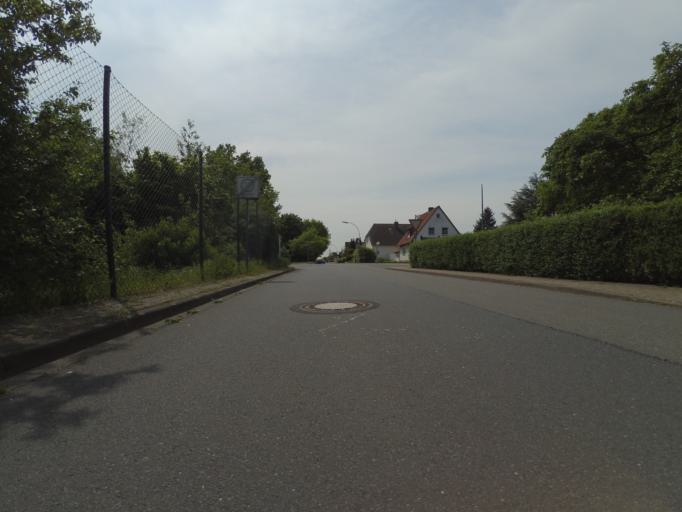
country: DE
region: Lower Saxony
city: Peine
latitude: 52.3357
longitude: 10.1832
